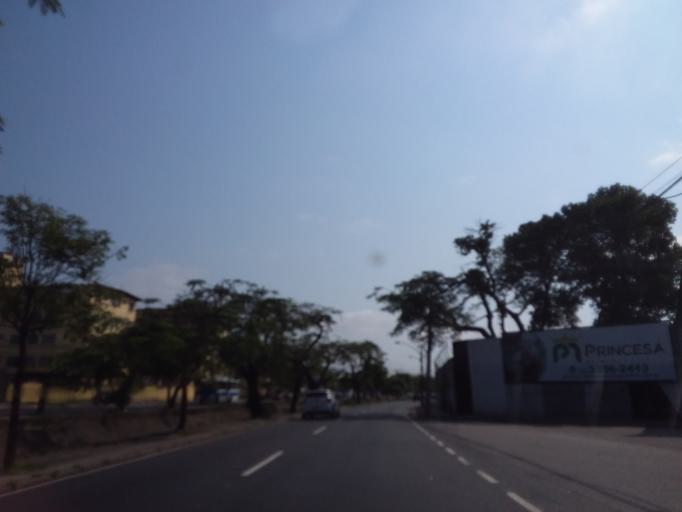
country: BR
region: Rio de Janeiro
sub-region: Nilopolis
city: Nilopolis
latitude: -22.9011
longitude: -43.5443
